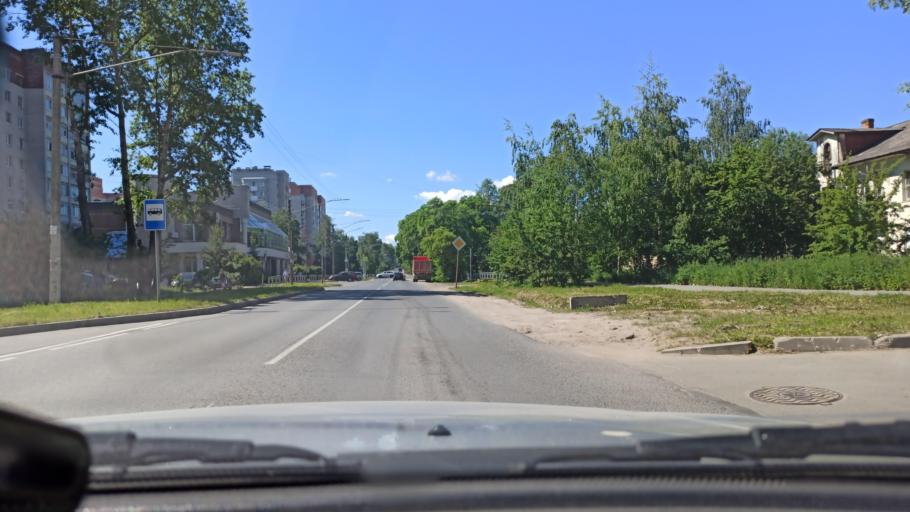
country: RU
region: Vologda
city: Vologda
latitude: 59.2165
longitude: 39.8483
